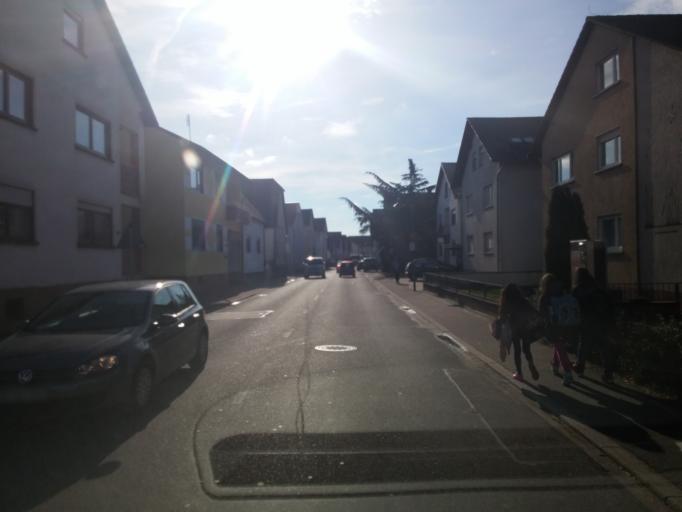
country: DE
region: Baden-Wuerttemberg
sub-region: Karlsruhe Region
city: Karlsdorf-Neuthard
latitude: 49.1325
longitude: 8.5234
